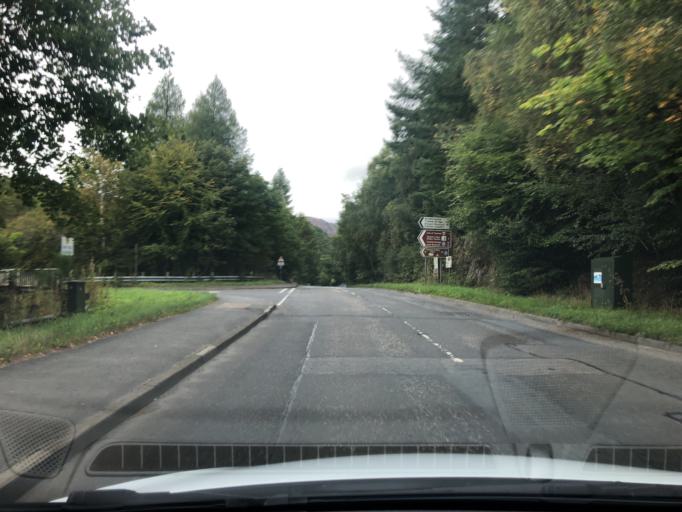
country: GB
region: Scotland
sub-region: Perth and Kinross
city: Pitlochry
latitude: 56.7276
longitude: -3.7743
